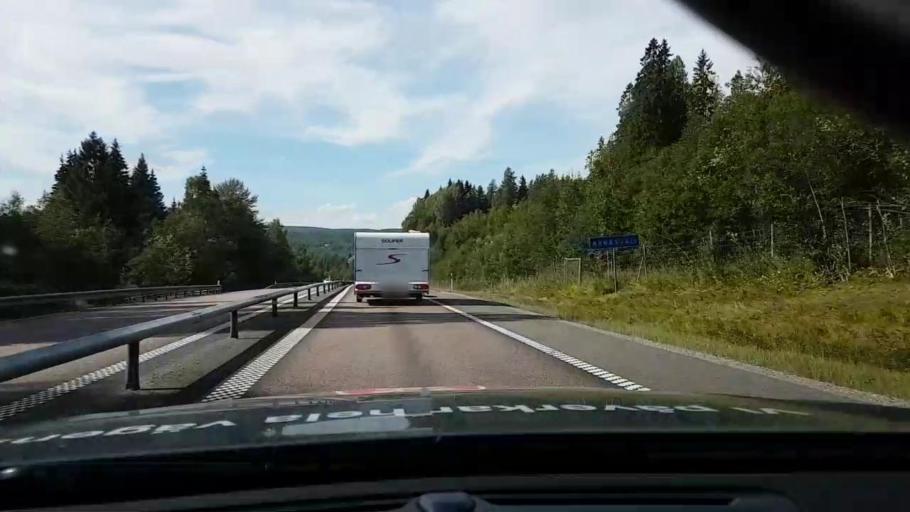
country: SE
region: Vaesternorrland
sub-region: OErnskoeldsviks Kommun
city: Ornskoldsvik
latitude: 63.3149
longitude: 18.8116
